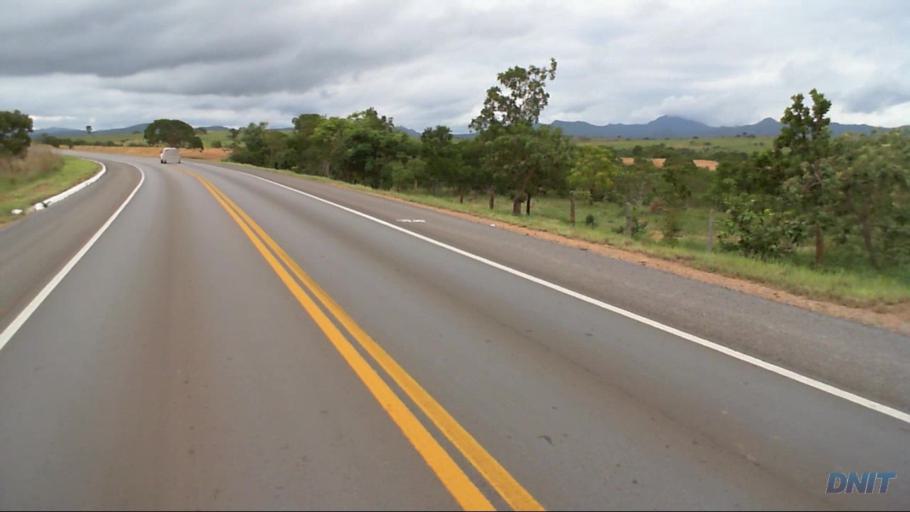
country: BR
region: Goias
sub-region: Padre Bernardo
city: Padre Bernardo
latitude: -15.2112
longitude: -48.5633
